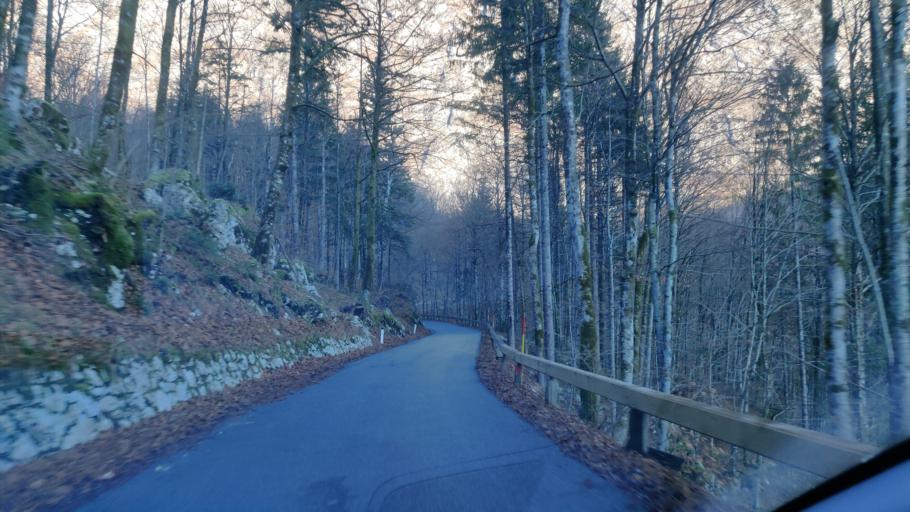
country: SI
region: Tolmin
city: Tolmin
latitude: 46.2847
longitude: 13.8073
